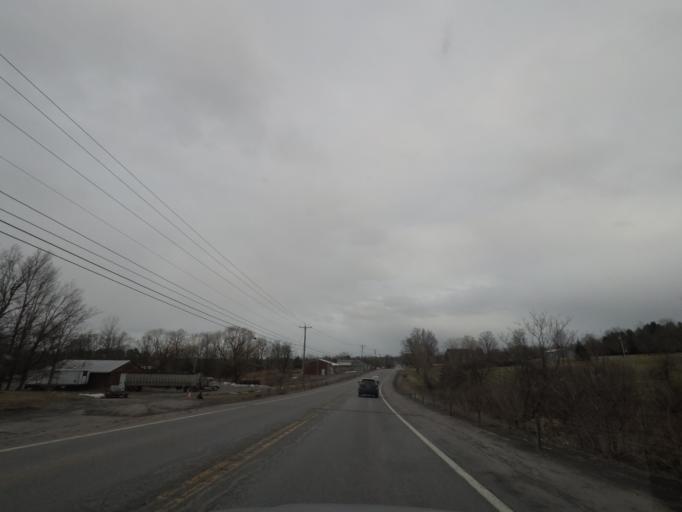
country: US
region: New York
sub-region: Madison County
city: Wampsville
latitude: 43.0740
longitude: -75.7238
